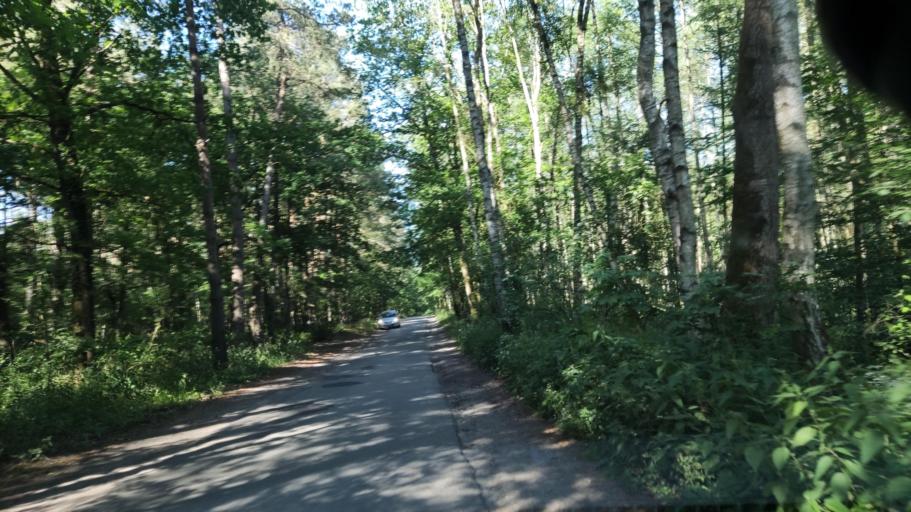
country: DE
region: Lower Saxony
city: Stelle
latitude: 53.3807
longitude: 10.0589
